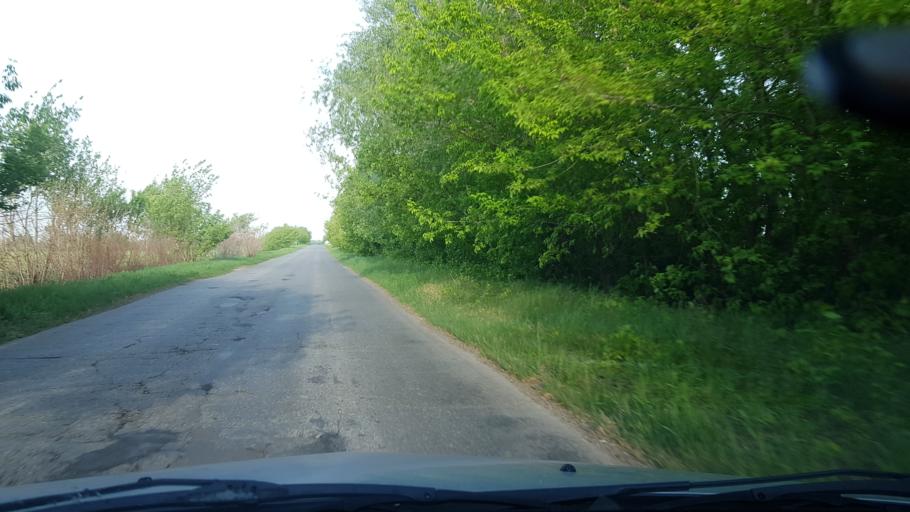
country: RU
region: Samara
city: Khryashchevka
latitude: 53.8268
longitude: 49.1264
